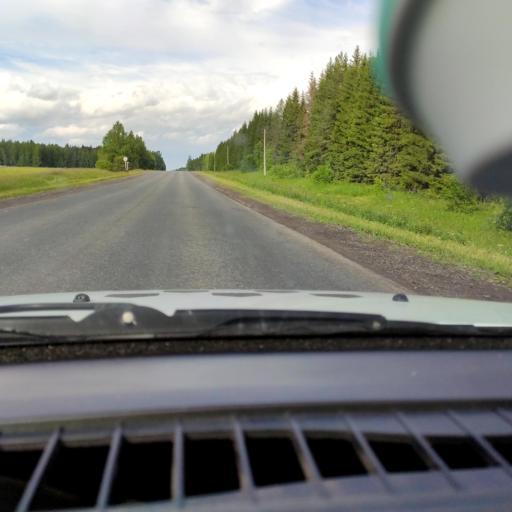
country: RU
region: Perm
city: Orda
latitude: 57.2304
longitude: 56.9677
